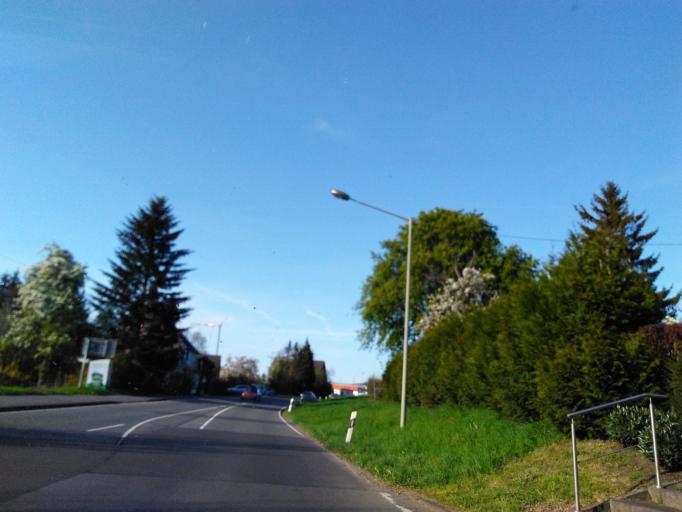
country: DE
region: North Rhine-Westphalia
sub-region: Regierungsbezirk Koln
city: Overath
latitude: 50.8638
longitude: 7.3159
